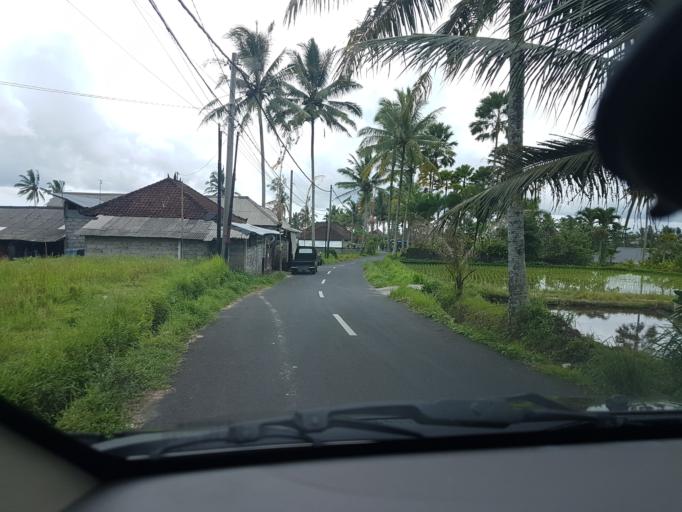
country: ID
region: Bali
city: Banjar Triwangsakeliki
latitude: -8.4610
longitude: 115.2743
